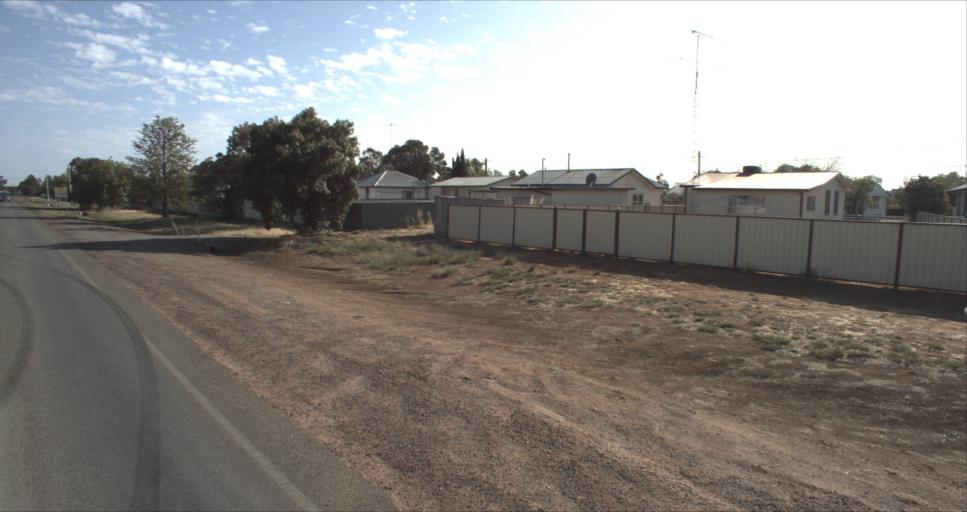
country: AU
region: New South Wales
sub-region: Leeton
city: Leeton
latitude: -34.5663
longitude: 146.3934
